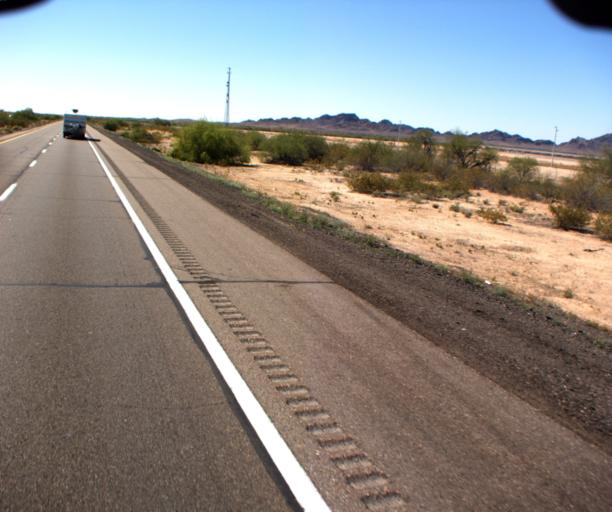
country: US
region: Arizona
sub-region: Maricopa County
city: Gila Bend
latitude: 32.9081
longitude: -112.9781
